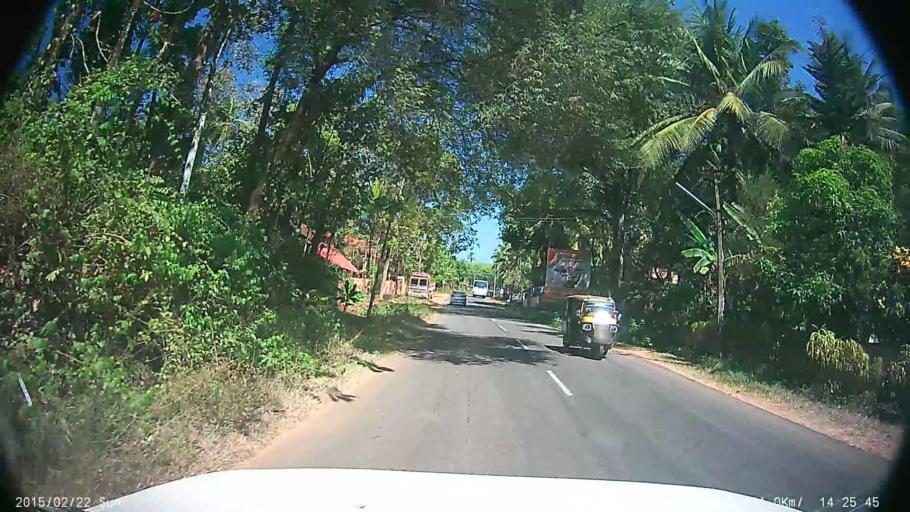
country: IN
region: Kerala
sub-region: Kottayam
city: Erattupetta
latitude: 9.5692
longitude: 76.7221
